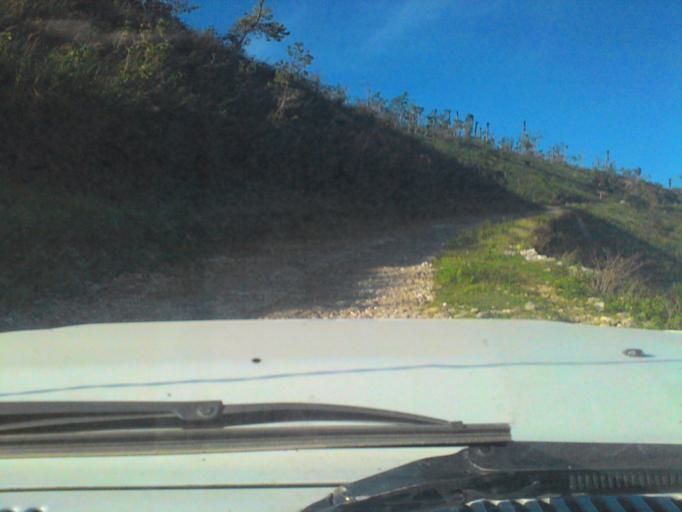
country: HT
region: Grandans
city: Jeremie
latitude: 18.5124
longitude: -74.0859
